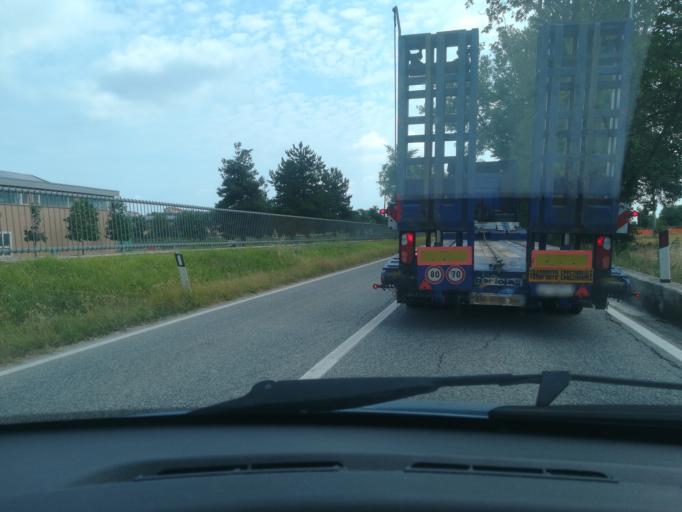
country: IT
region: The Marches
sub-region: Provincia di Macerata
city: Recanati
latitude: 43.3750
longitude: 13.5236
